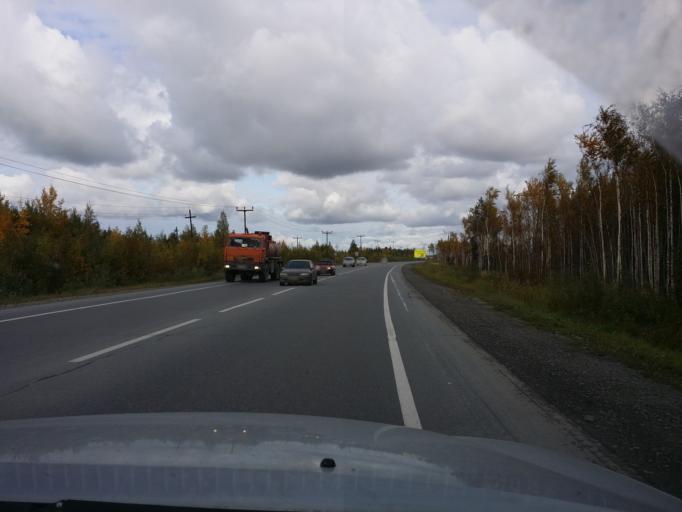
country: RU
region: Khanty-Mansiyskiy Avtonomnyy Okrug
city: Nizhnevartovsk
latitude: 61.0277
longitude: 76.3649
